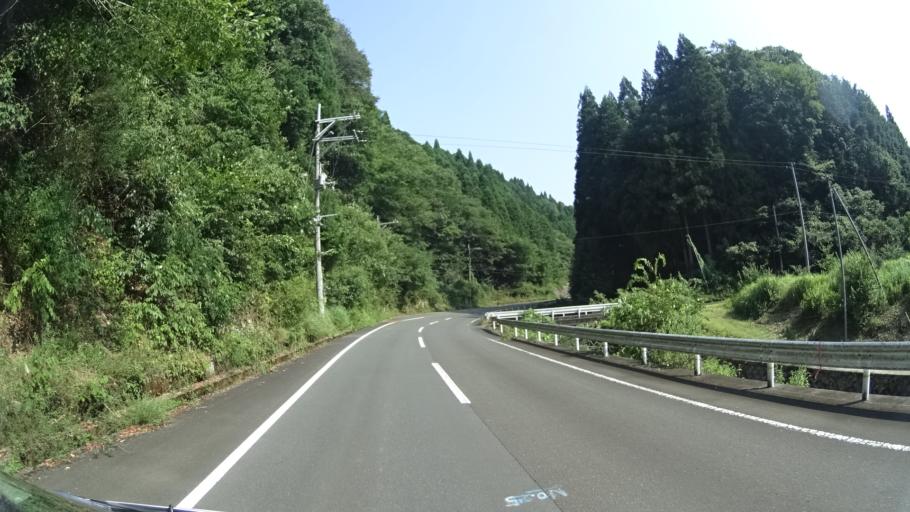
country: JP
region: Kyoto
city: Maizuru
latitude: 35.4157
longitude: 135.2297
